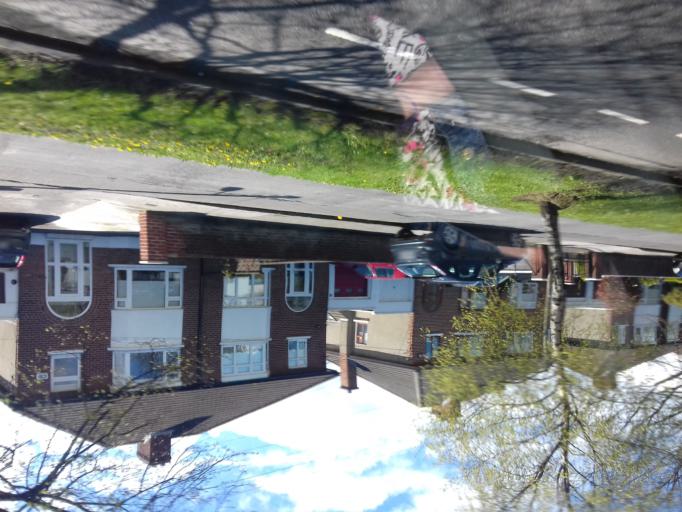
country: IE
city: Coolock
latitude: 53.3871
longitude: -6.2004
